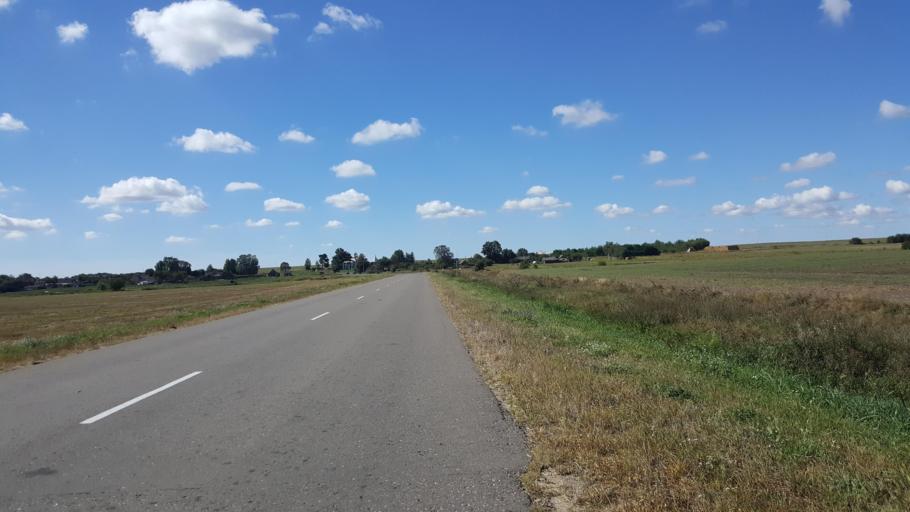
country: BY
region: Brest
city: Vysokaye
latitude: 52.3606
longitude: 23.5140
